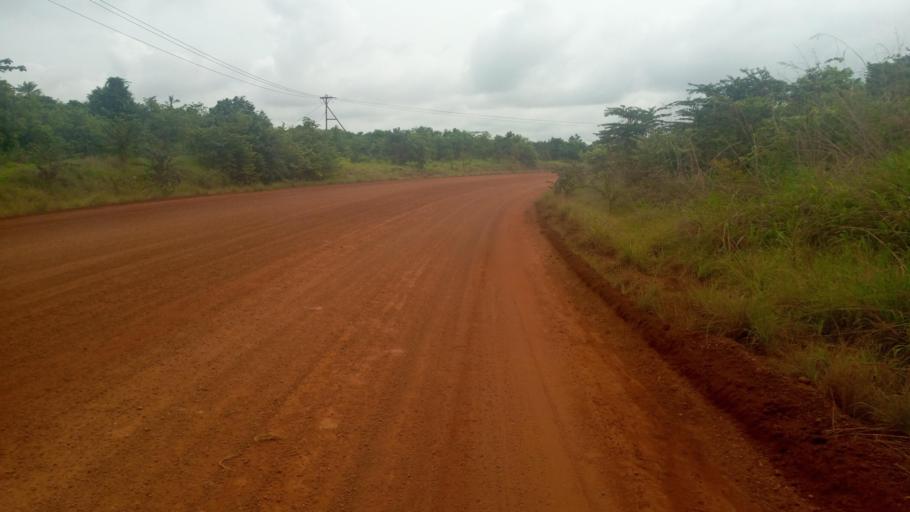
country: SL
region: Southern Province
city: Mogbwemo
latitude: 7.7206
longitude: -12.2857
